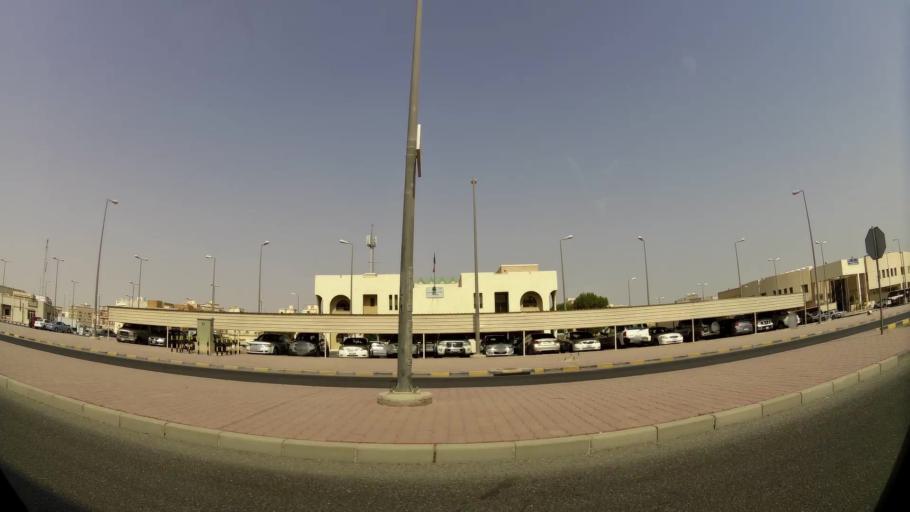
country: KW
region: Muhafazat al Jahra'
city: Al Jahra'
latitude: 29.3065
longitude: 47.6974
